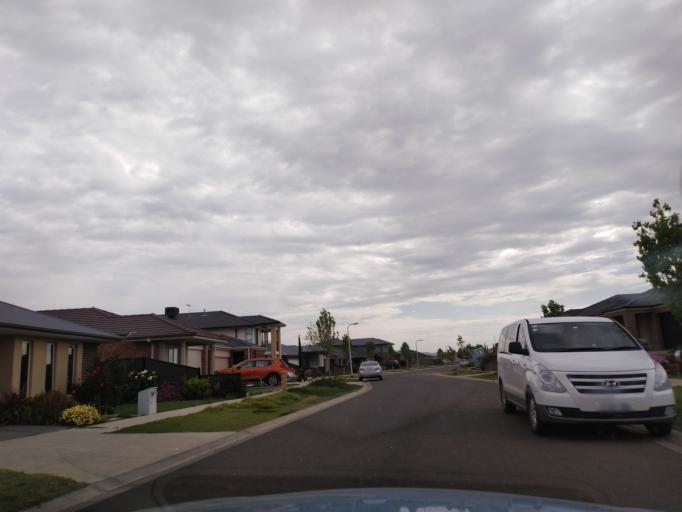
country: AU
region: Victoria
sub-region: Wyndham
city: Williams Landing
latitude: -37.8458
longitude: 144.7153
